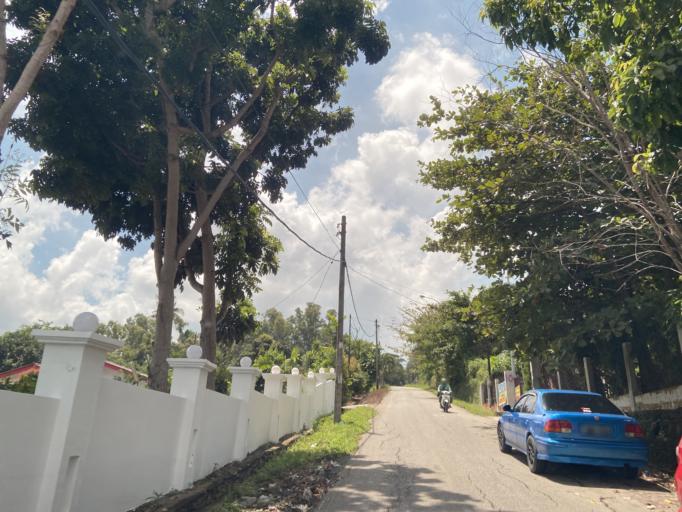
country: SG
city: Singapore
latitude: 1.1523
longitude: 104.0123
